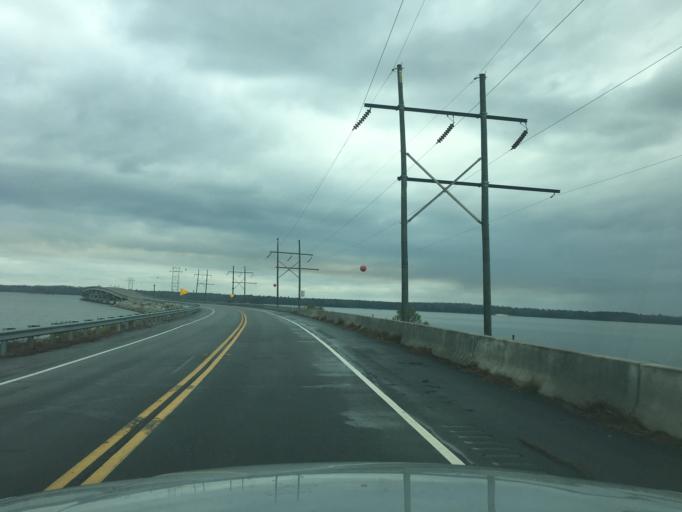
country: US
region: Georgia
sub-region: Columbia County
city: Appling
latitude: 33.6888
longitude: -82.3342
